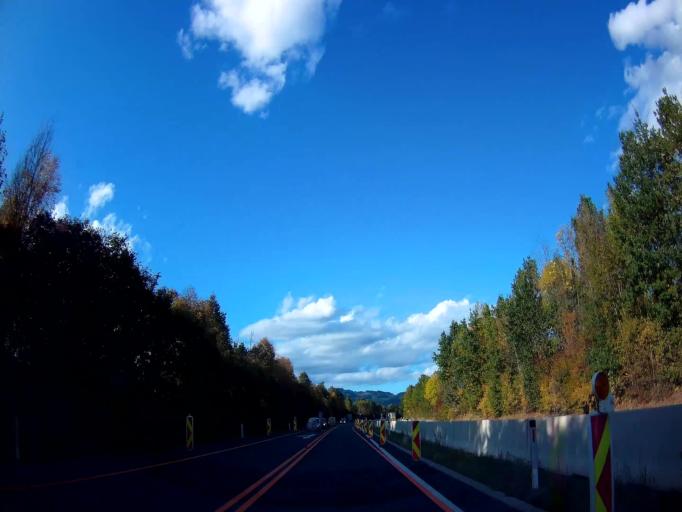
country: AT
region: Carinthia
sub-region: Politischer Bezirk Wolfsberg
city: Wolfsberg
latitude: 46.8253
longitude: 14.8190
